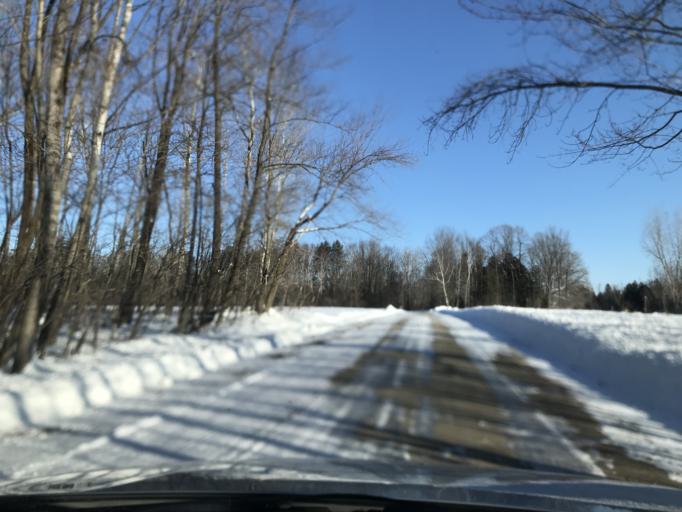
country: US
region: Wisconsin
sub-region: Oconto County
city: Oconto
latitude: 44.9557
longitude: -87.9769
